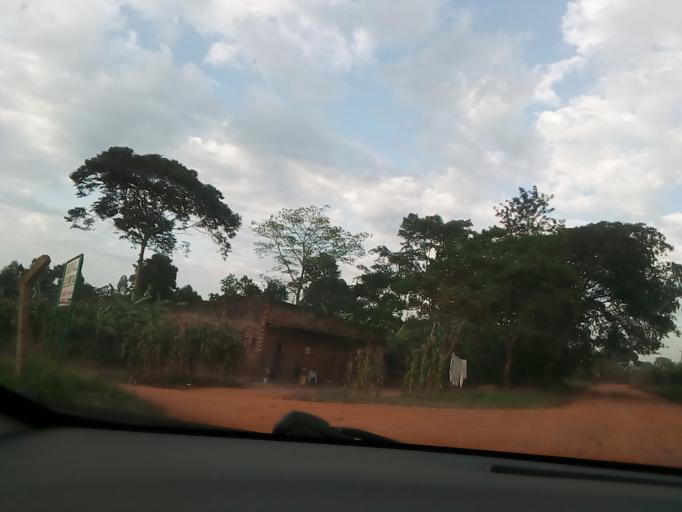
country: UG
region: Central Region
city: Masaka
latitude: -0.3440
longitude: 31.7072
